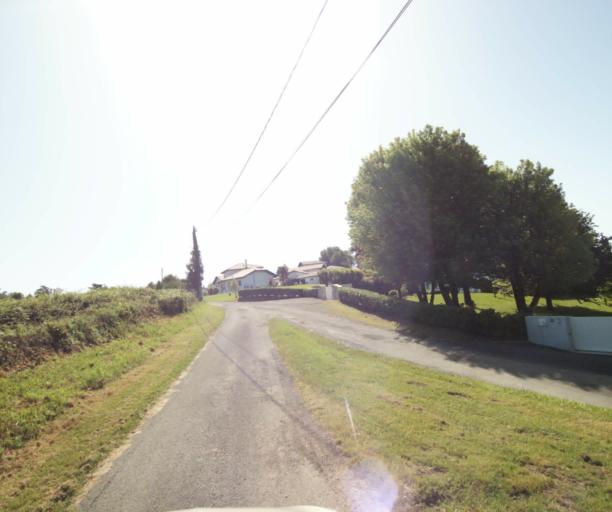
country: FR
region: Aquitaine
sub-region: Departement des Pyrenees-Atlantiques
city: Villefranque
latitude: 43.4530
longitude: -1.4478
